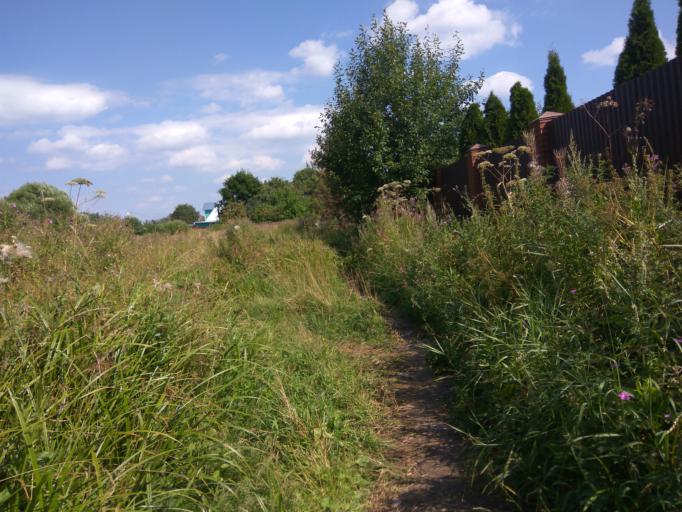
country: RU
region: Moskovskaya
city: Kubinka
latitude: 55.5862
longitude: 36.7507
